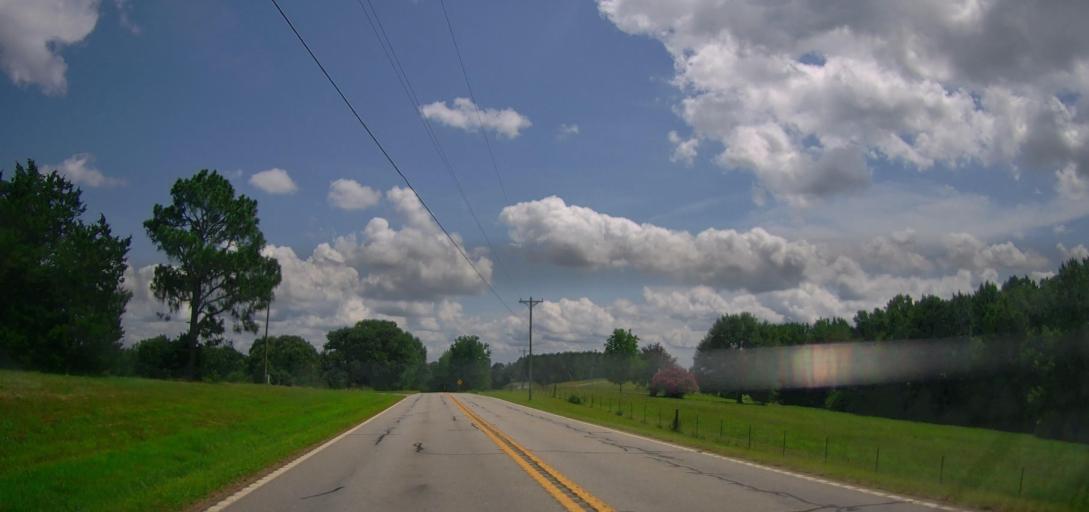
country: US
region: Georgia
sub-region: Carroll County
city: Bowdon
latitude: 33.4234
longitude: -85.2672
